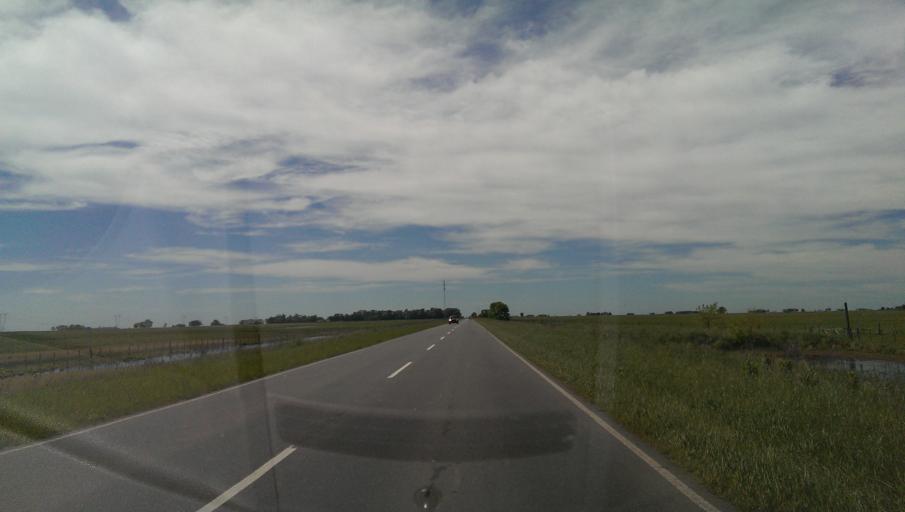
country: AR
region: Buenos Aires
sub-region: Partido de Laprida
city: Laprida
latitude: -37.2000
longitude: -60.6699
